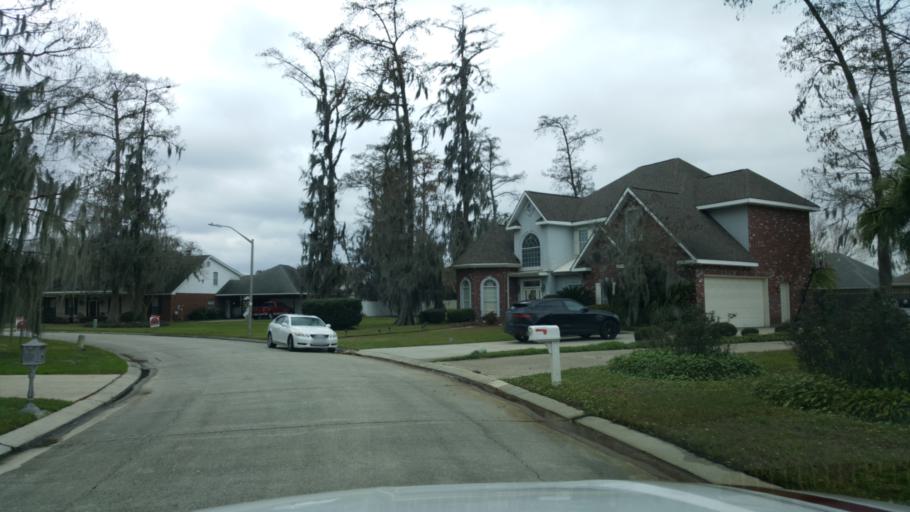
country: US
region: Louisiana
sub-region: Jefferson Parish
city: Woodmere
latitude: 29.8737
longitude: -90.0781
